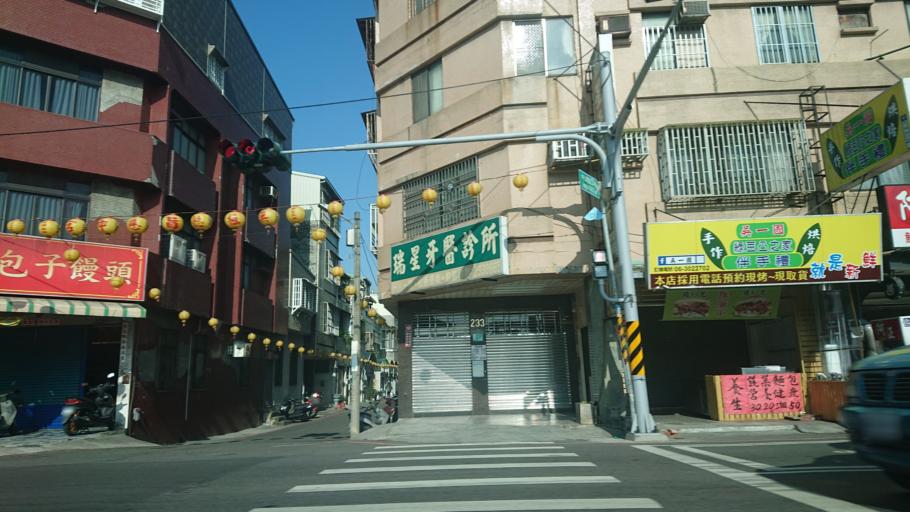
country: TW
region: Taiwan
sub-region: Tainan
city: Tainan
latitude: 23.0155
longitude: 120.2357
